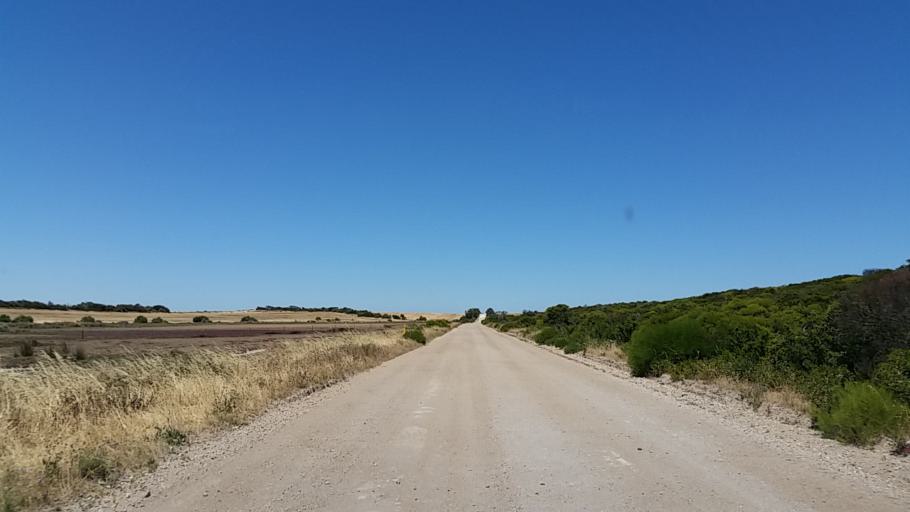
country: AU
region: South Australia
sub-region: Yorke Peninsula
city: Honiton
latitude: -35.0944
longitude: 137.4256
